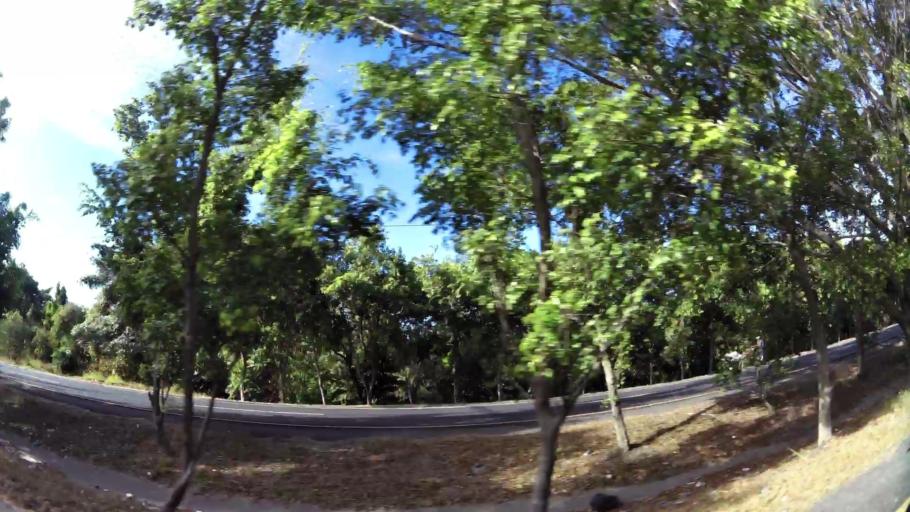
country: SV
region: Cuscatlan
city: Tecoluca
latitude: 13.7373
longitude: -89.0420
